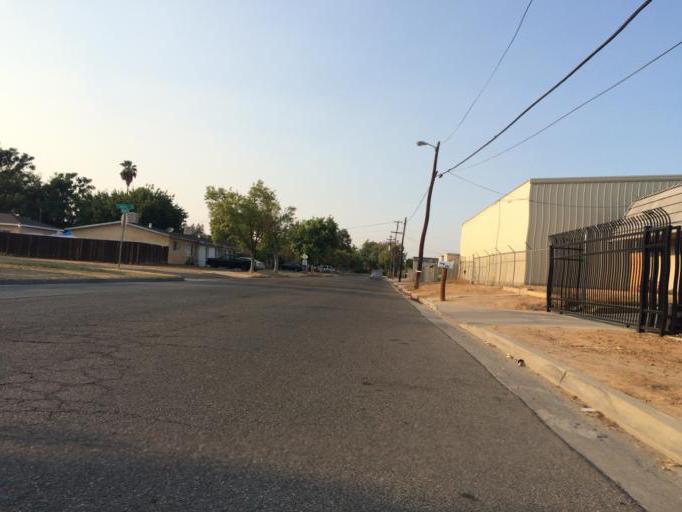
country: US
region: California
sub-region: Fresno County
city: Fresno
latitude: 36.8406
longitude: -119.8107
